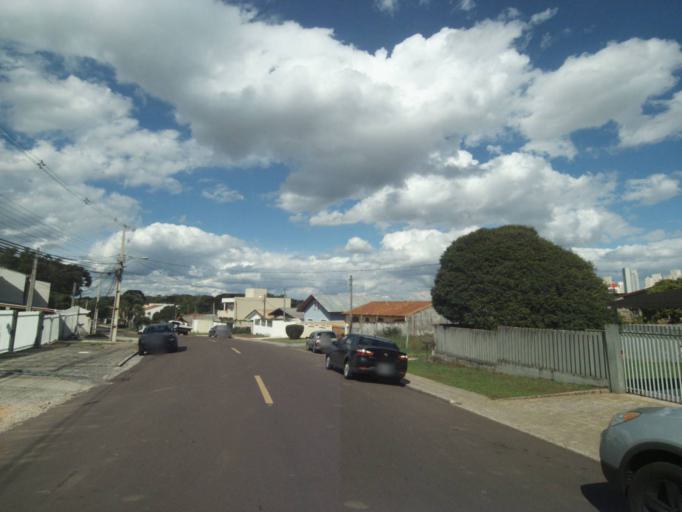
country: BR
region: Parana
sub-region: Curitiba
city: Curitiba
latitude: -25.4373
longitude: -49.3475
